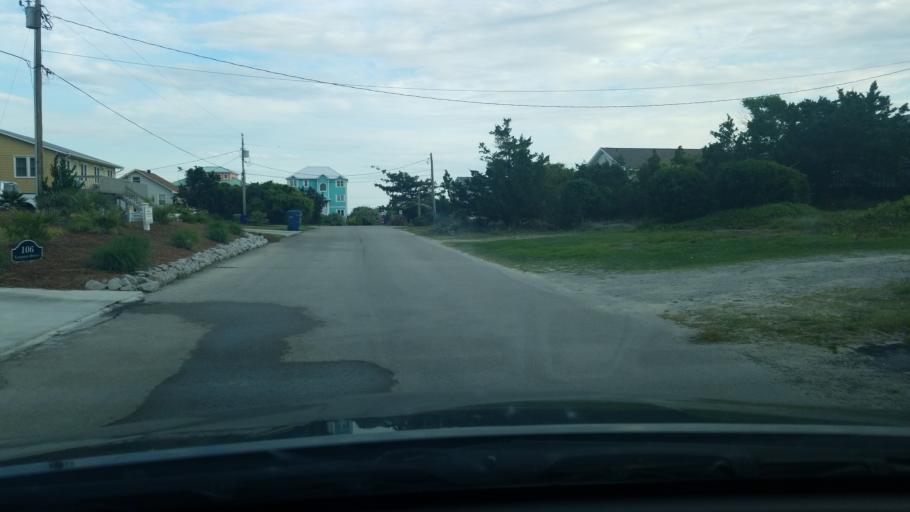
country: US
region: North Carolina
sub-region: Carteret County
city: Cape Carteret
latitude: 34.6600
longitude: -77.0450
